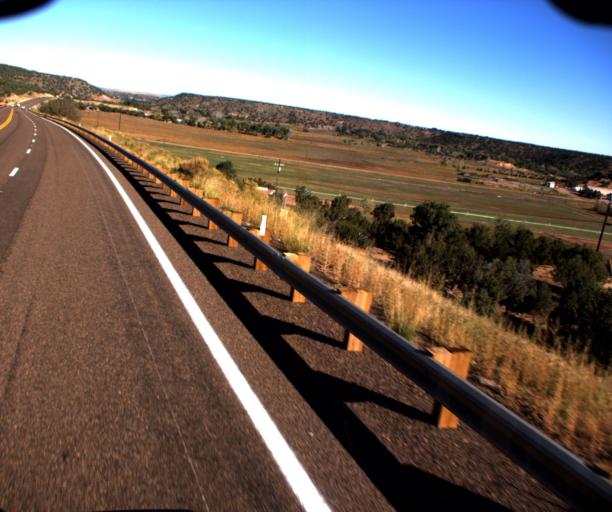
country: US
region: Arizona
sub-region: Navajo County
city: White Mountain Lake
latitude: 34.3745
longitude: -110.0525
